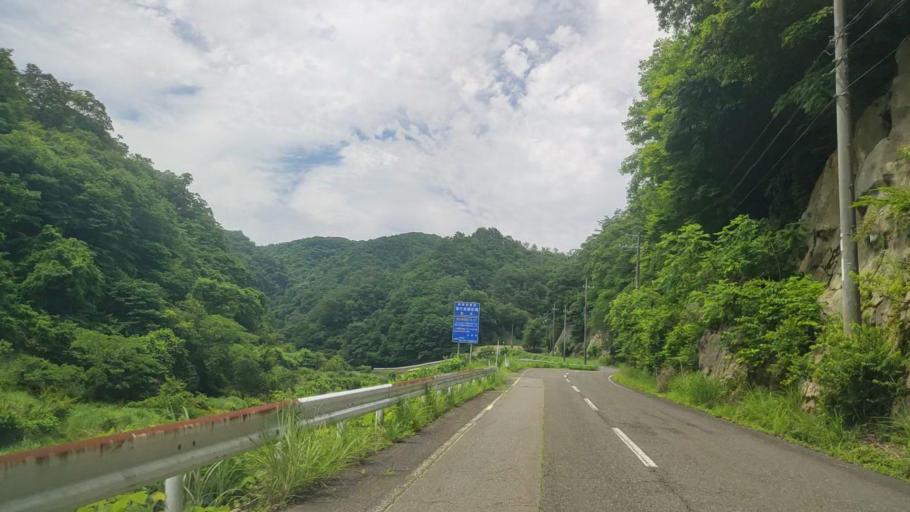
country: JP
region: Hyogo
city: Toyooka
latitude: 35.5223
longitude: 134.6972
